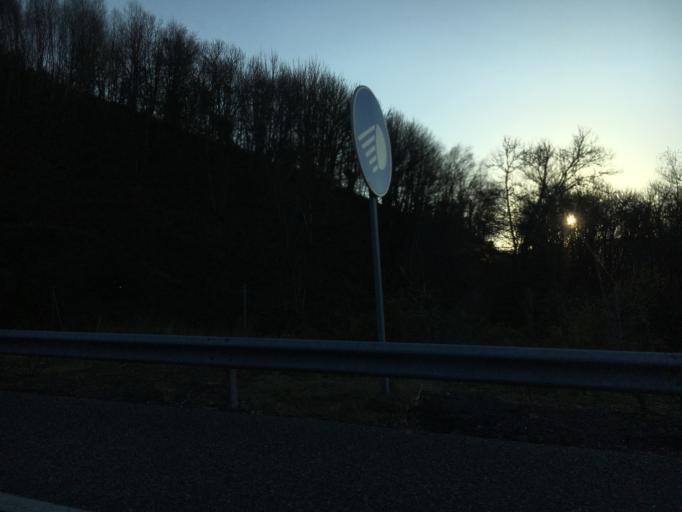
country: ES
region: Galicia
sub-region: Provincia de Lugo
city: Becerrea
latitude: 42.7897
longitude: -7.1099
